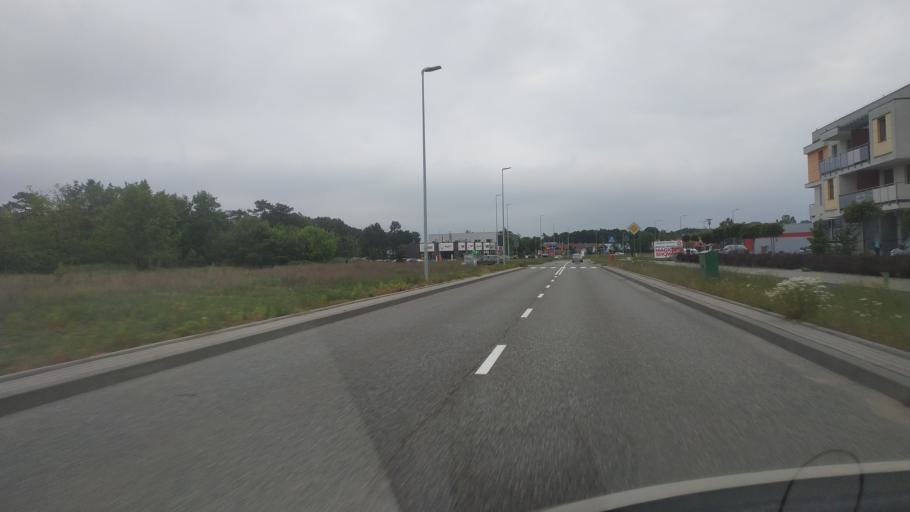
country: PL
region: Kujawsko-Pomorskie
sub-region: Torun
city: Torun
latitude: 53.0430
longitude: 18.6005
